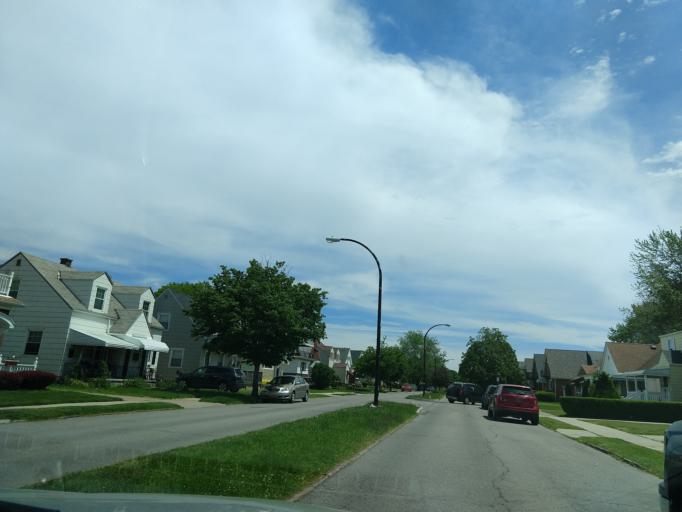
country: US
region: New York
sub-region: Erie County
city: Lackawanna
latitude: 42.8396
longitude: -78.8217
